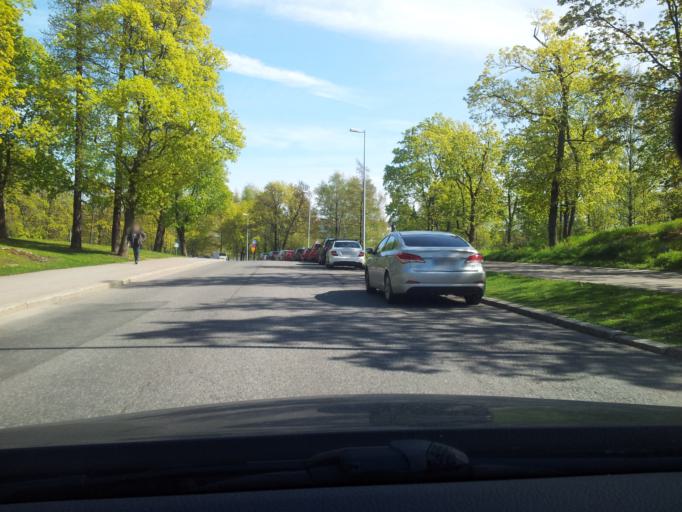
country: FI
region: Uusimaa
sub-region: Helsinki
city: Helsinki
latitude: 60.1814
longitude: 24.9405
